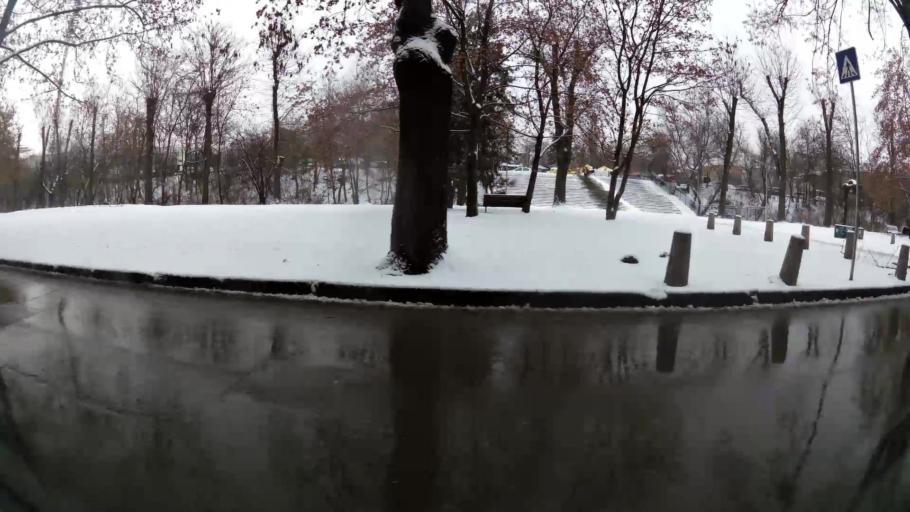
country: BG
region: Sofia-Capital
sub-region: Stolichna Obshtina
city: Sofia
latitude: 42.6875
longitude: 23.3322
